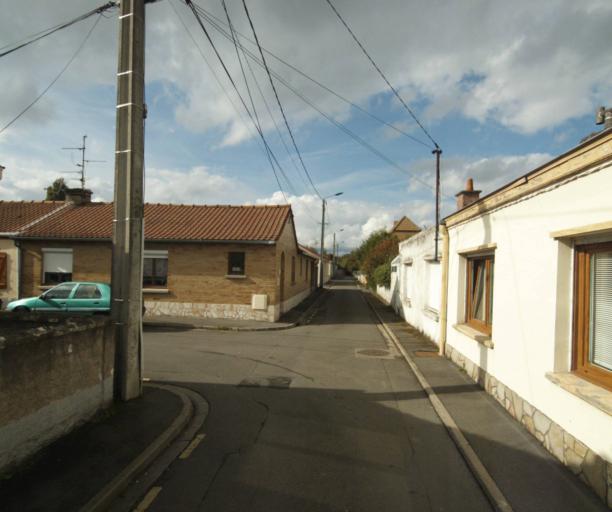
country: FR
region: Nord-Pas-de-Calais
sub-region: Departement du Nord
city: Wavrin
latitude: 50.5702
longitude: 2.9411
